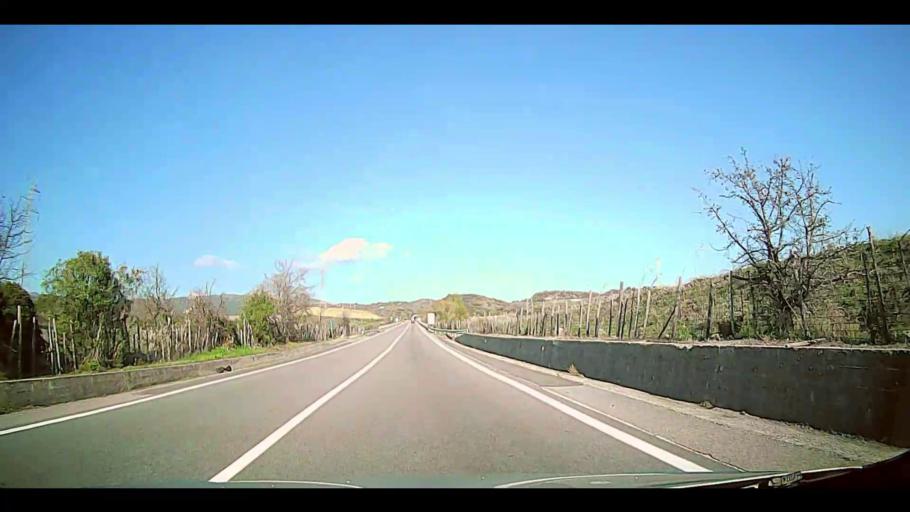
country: IT
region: Calabria
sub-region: Provincia di Crotone
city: Cotronei
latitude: 39.1881
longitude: 16.8171
